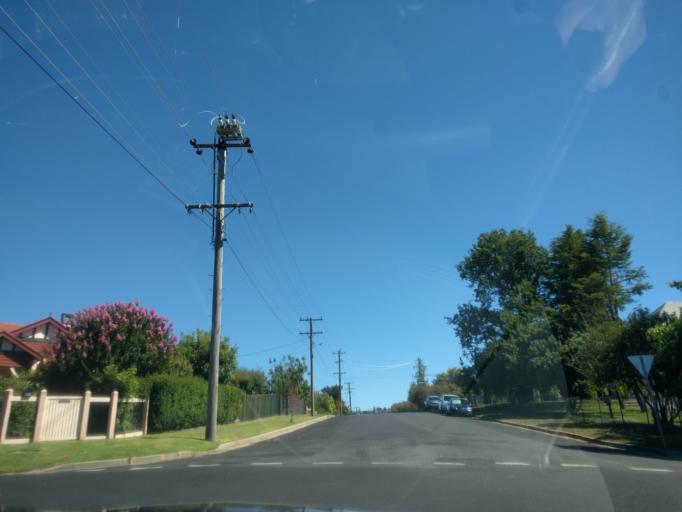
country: AU
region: New South Wales
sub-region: Armidale Dumaresq
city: Armidale
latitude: -30.5226
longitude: 151.6639
